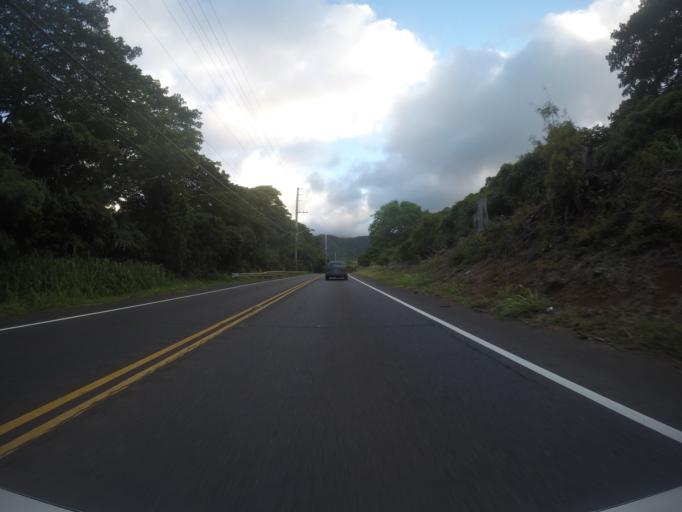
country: US
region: Hawaii
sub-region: Honolulu County
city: Ka'a'awa
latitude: 21.5133
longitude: -157.8476
